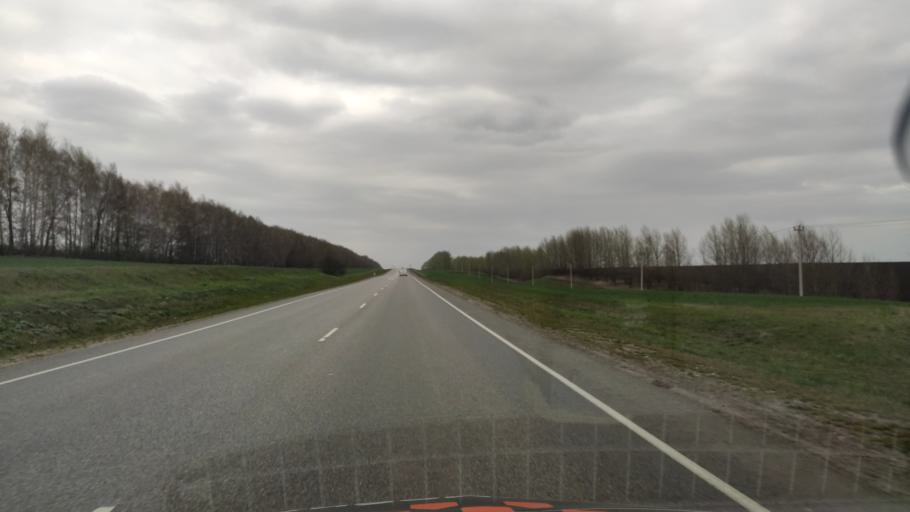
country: RU
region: Kursk
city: Gorshechnoye
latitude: 51.5486
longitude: 38.1230
